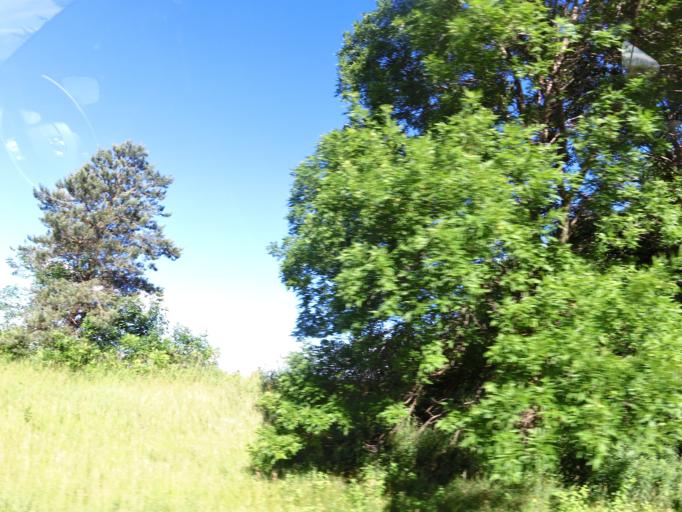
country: US
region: Minnesota
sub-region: Dakota County
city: Hastings
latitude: 44.8180
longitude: -92.8629
